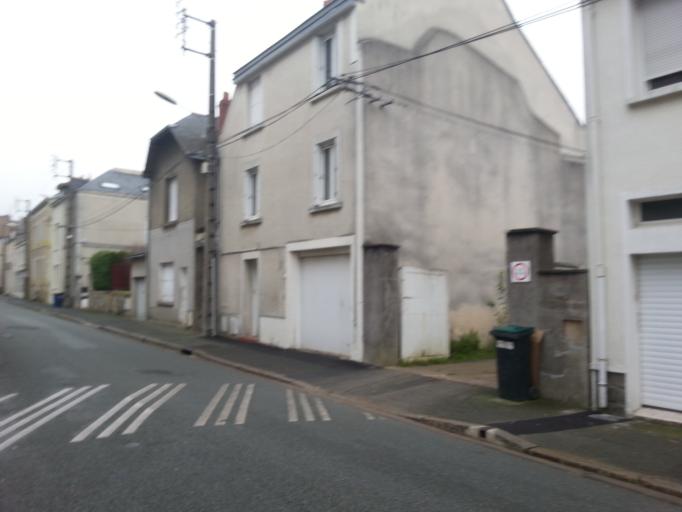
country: FR
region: Pays de la Loire
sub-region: Departement de Maine-et-Loire
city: Angers
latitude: 47.4607
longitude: -0.5587
